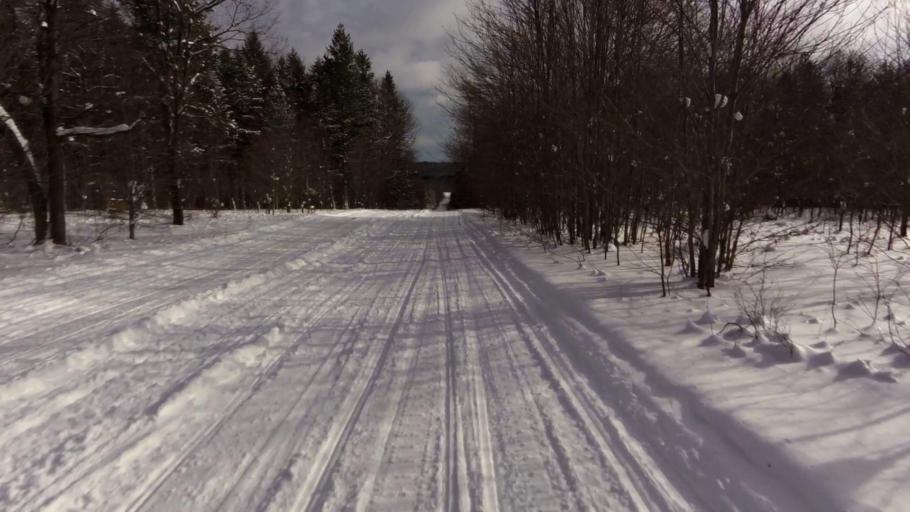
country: US
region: New York
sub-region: Cattaraugus County
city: Franklinville
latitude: 42.3045
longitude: -78.5251
